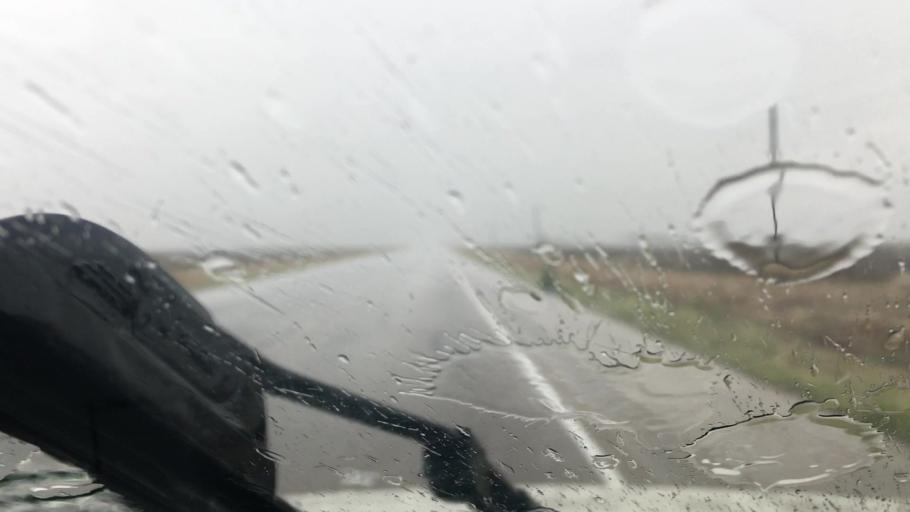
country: US
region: New Mexico
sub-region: Lea County
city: Lovington
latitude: 33.2570
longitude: -103.2183
